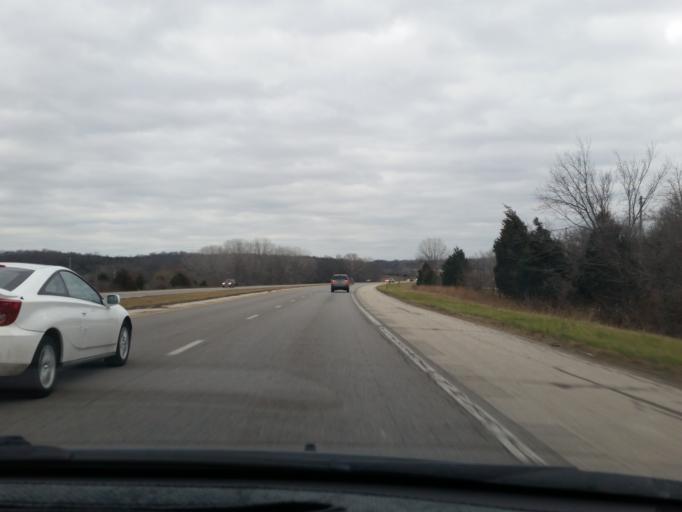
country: US
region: Kansas
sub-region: Johnson County
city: De Soto
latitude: 38.9559
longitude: -94.9146
